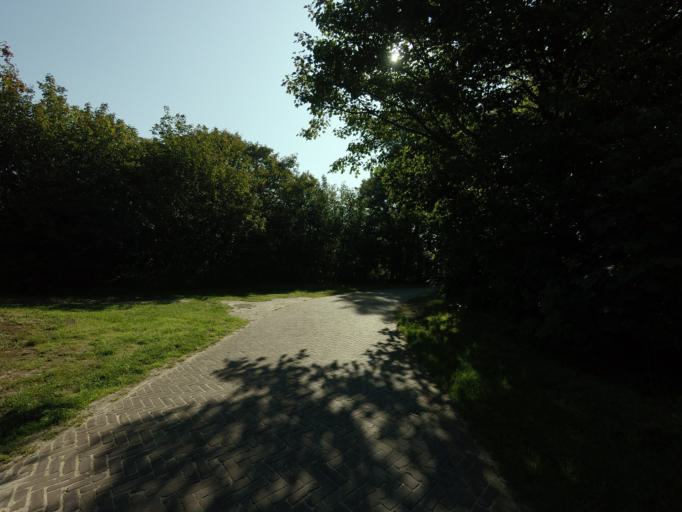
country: NL
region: Friesland
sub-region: Gemeente Schiermonnikoog
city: Schiermonnikoog
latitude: 53.4820
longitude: 6.1662
